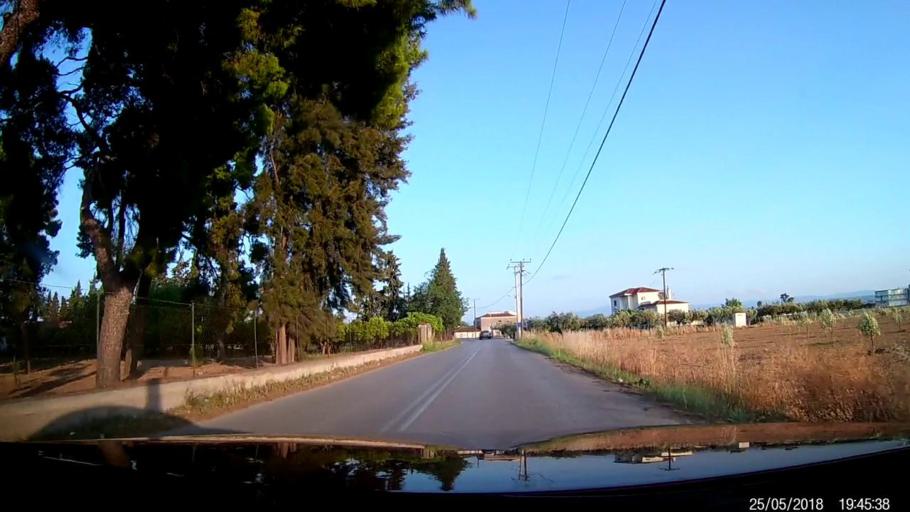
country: GR
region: Central Greece
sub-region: Nomos Evvoias
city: Ayios Nikolaos
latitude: 38.4315
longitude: 23.6344
